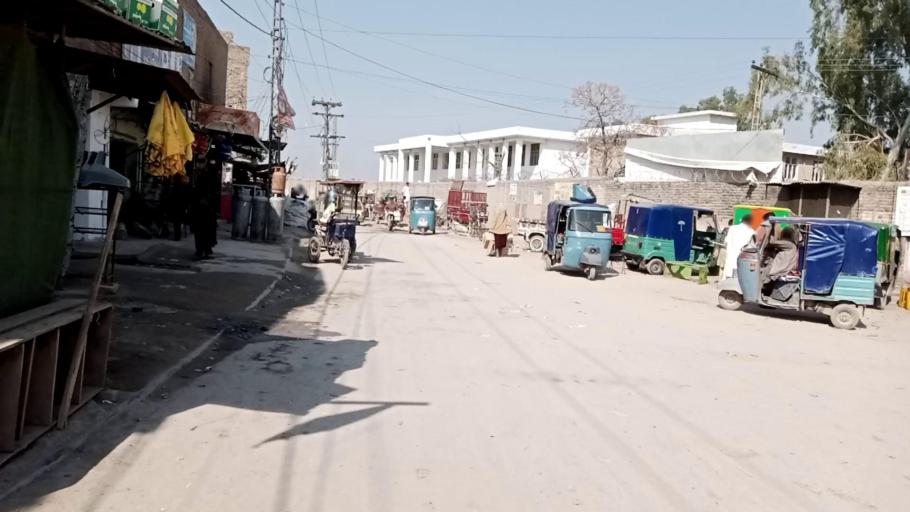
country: PK
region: Khyber Pakhtunkhwa
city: Peshawar
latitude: 34.0130
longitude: 71.5136
